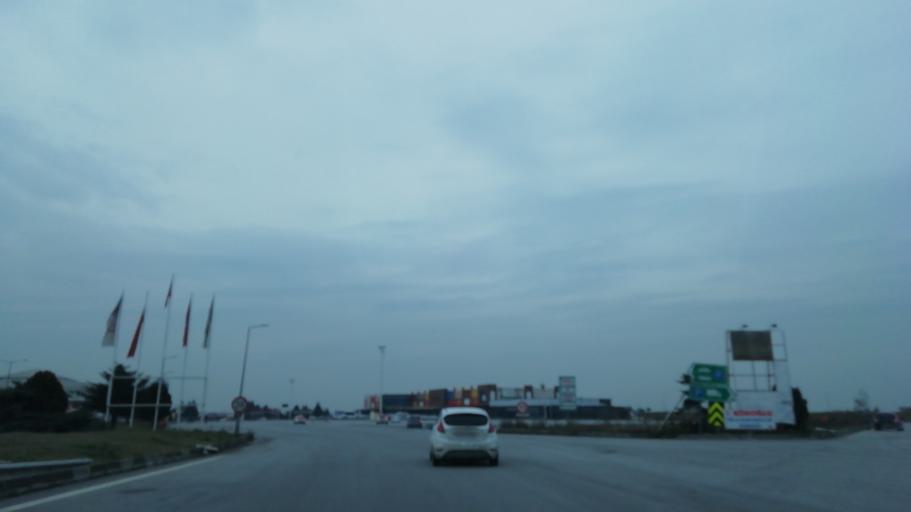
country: TR
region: Duzce
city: Kaynasli
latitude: 40.7907
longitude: 31.2440
